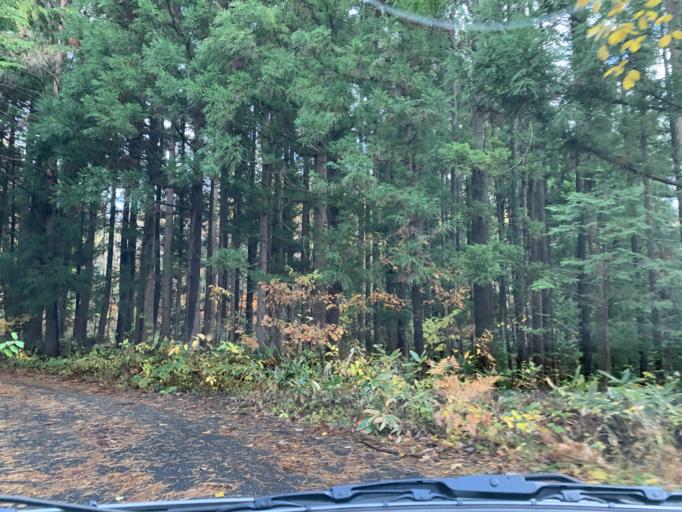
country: JP
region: Iwate
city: Mizusawa
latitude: 39.1024
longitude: 140.9675
